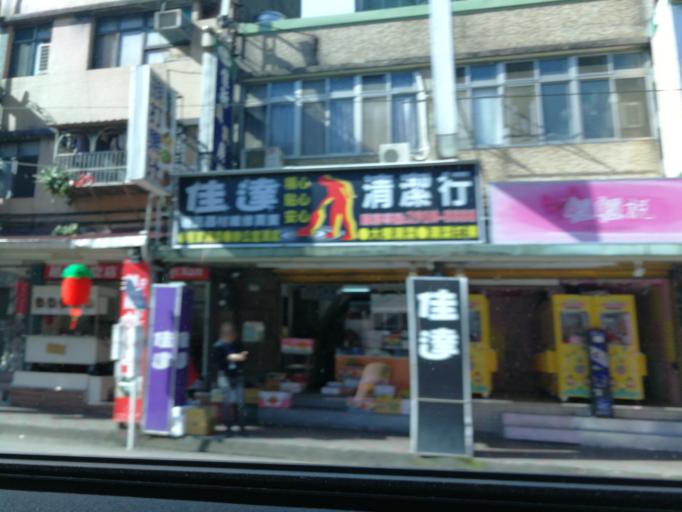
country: TW
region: Taipei
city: Taipei
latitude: 24.9566
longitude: 121.5383
